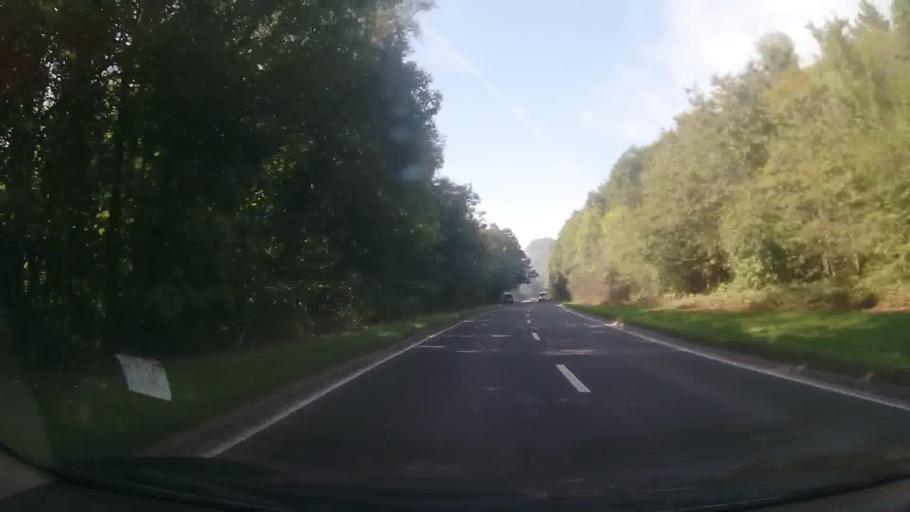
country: GB
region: England
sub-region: Herefordshire
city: Kington
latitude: 52.2063
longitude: -3.0364
